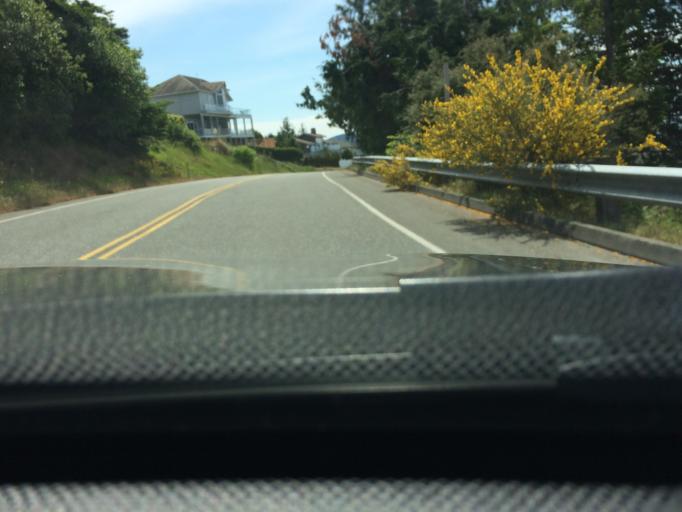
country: US
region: Washington
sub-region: Skagit County
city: Anacortes
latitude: 48.4931
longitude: -122.6706
